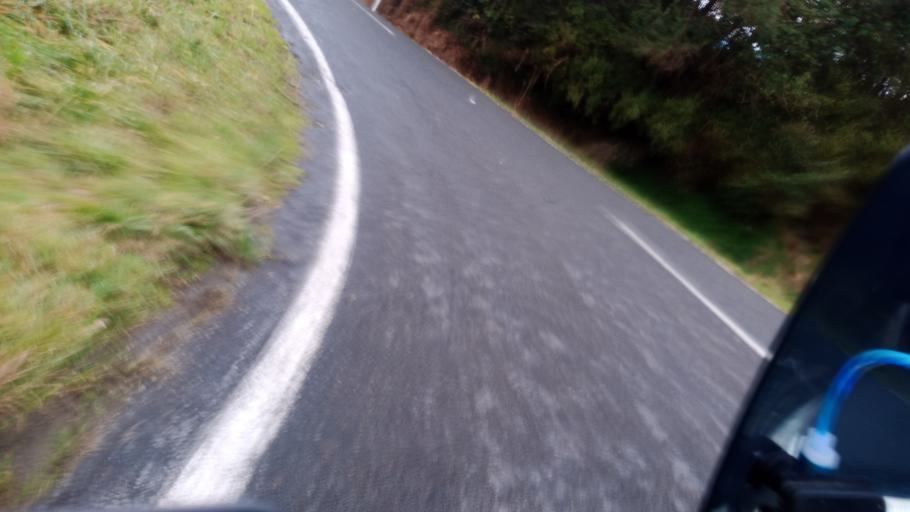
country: NZ
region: Gisborne
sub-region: Gisborne District
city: Gisborne
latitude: -38.3199
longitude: 178.3169
